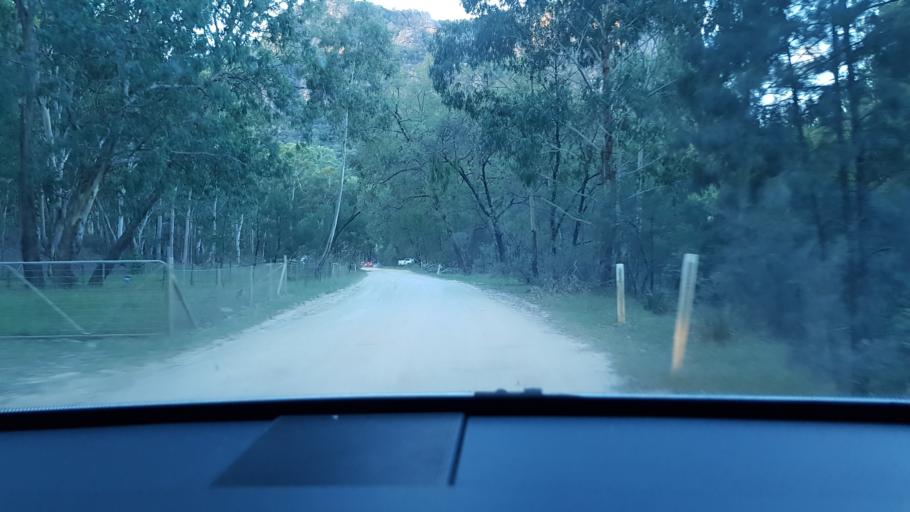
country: AU
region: New South Wales
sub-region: Lithgow
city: Portland
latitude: -33.1756
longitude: 150.2366
